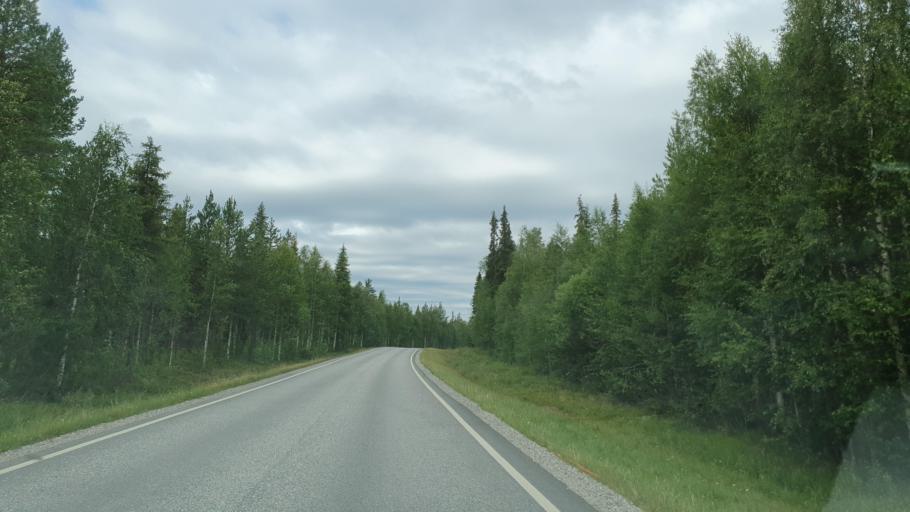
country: FI
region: Lapland
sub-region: Tunturi-Lappi
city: Kittilae
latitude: 67.5786
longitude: 25.5916
